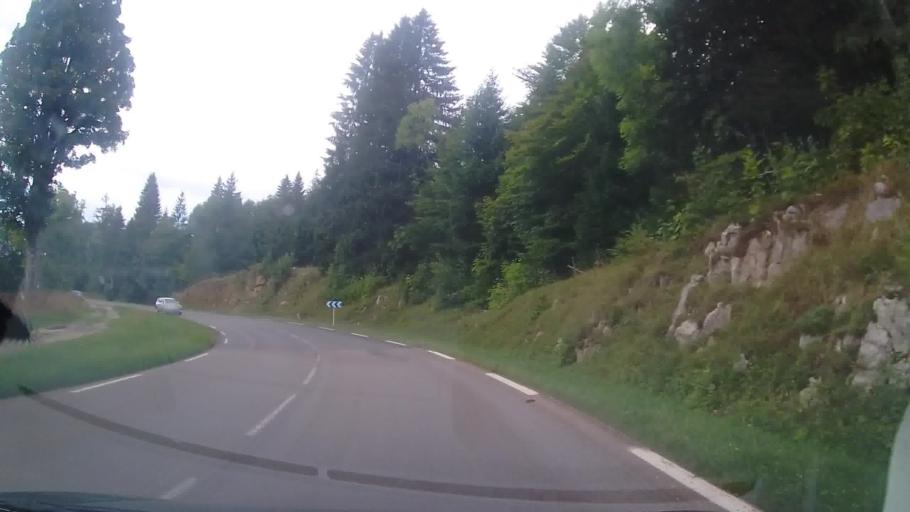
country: FR
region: Franche-Comte
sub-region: Departement du Jura
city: Les Rousses
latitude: 46.4578
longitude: 6.0753
